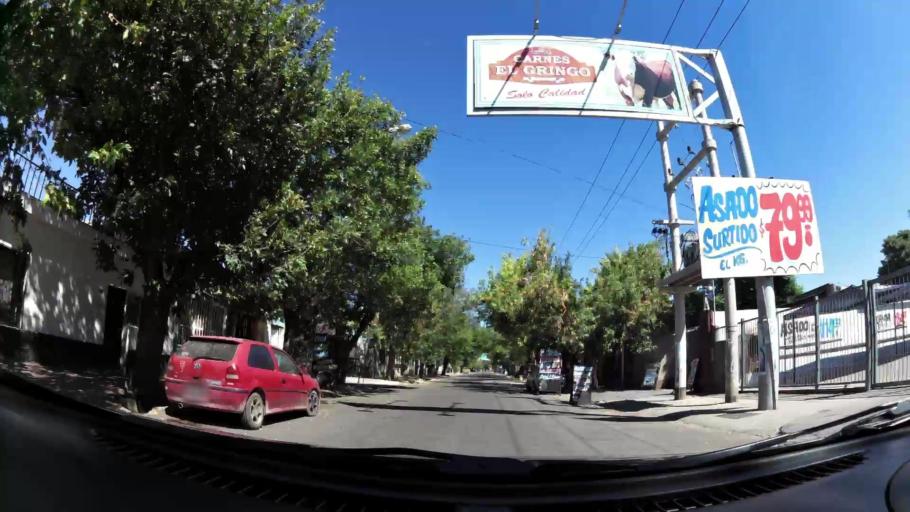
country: AR
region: Mendoza
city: Las Heras
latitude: -32.8480
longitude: -68.8413
